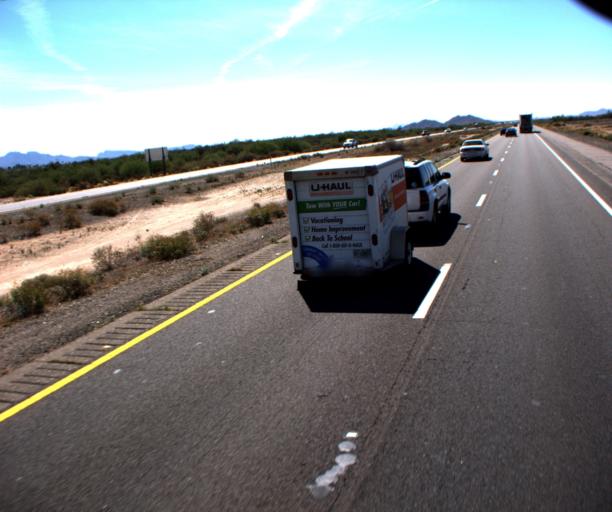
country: US
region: Arizona
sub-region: Maricopa County
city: Sun Lakes
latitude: 33.2091
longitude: -111.9125
